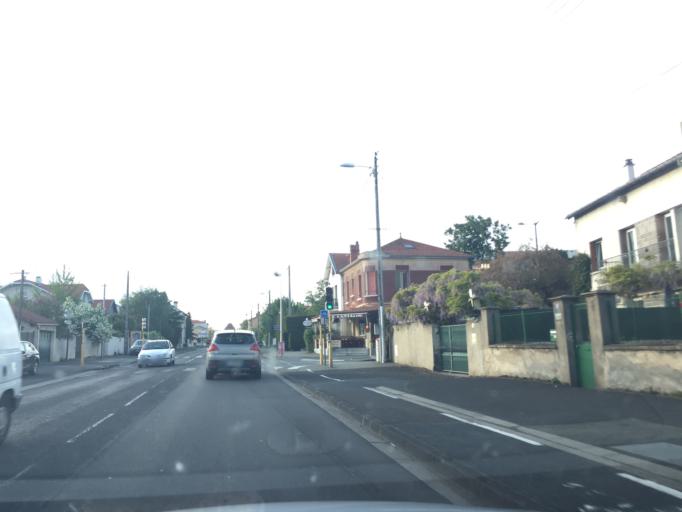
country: FR
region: Auvergne
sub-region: Departement du Puy-de-Dome
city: Riom
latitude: 45.8838
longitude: 3.1157
